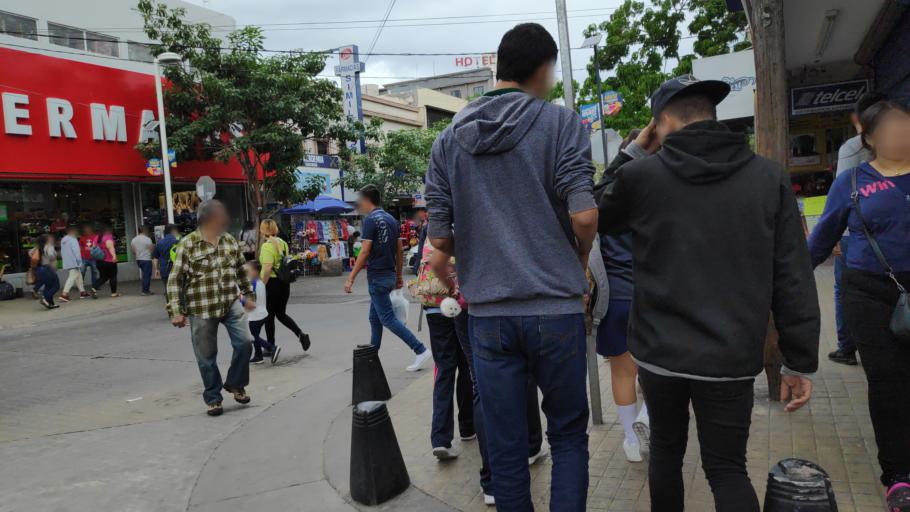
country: MX
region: Sinaloa
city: Culiacan
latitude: 24.8073
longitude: -107.3964
